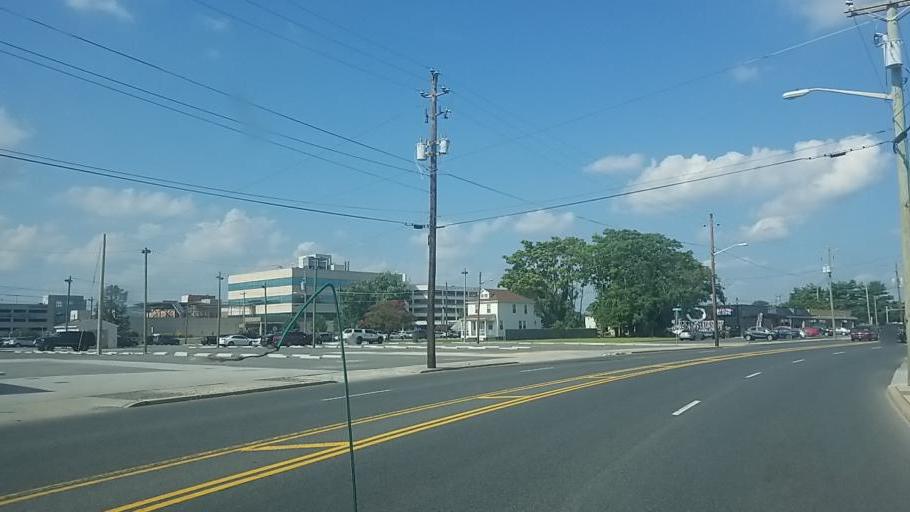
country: US
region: Maryland
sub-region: Wicomico County
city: Salisbury
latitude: 38.3588
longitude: -75.5992
